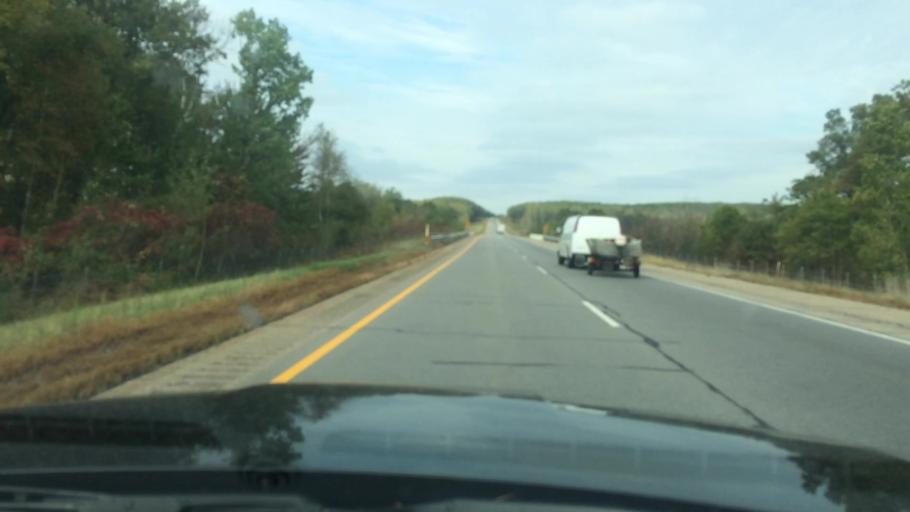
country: US
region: Wisconsin
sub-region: Marathon County
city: Mosinee
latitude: 44.6936
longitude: -89.6433
